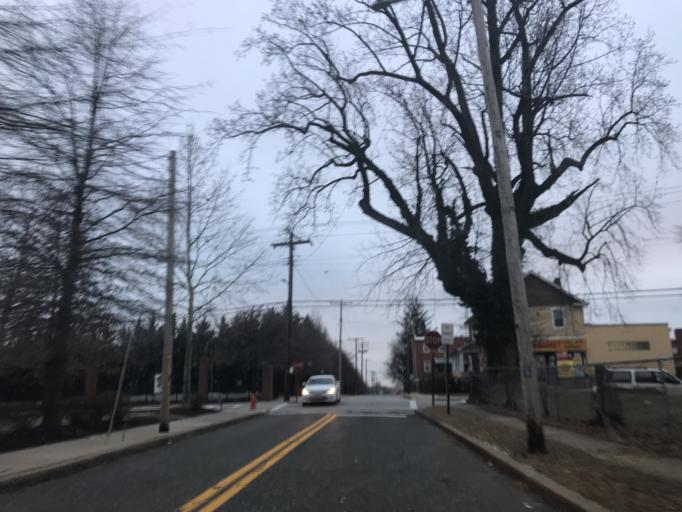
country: US
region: Maryland
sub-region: Baltimore County
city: Lochearn
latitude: 39.3544
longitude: -76.6792
